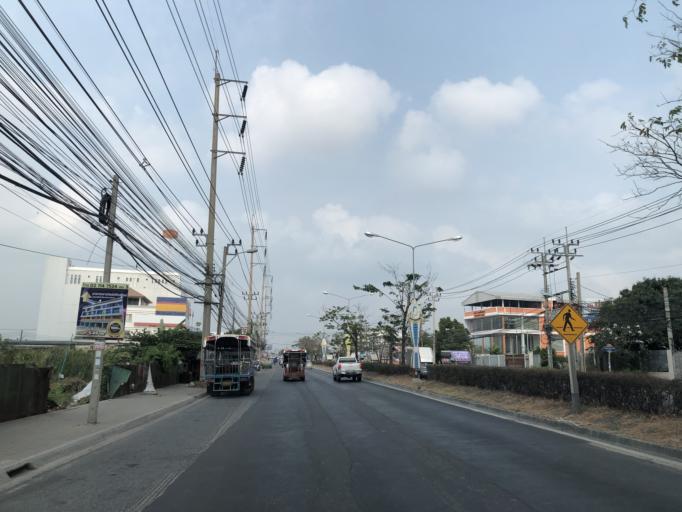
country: TH
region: Samut Prakan
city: Bang Bo District
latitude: 13.5958
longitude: 100.7516
